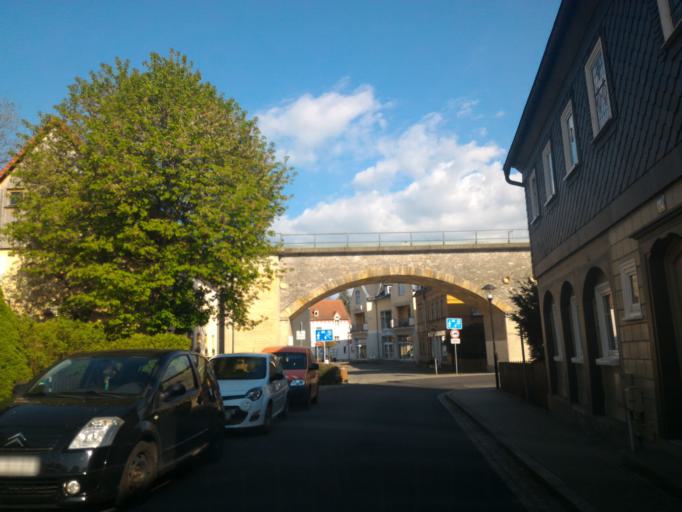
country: DE
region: Saxony
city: Seifhennersdorf
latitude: 50.9335
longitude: 14.6112
